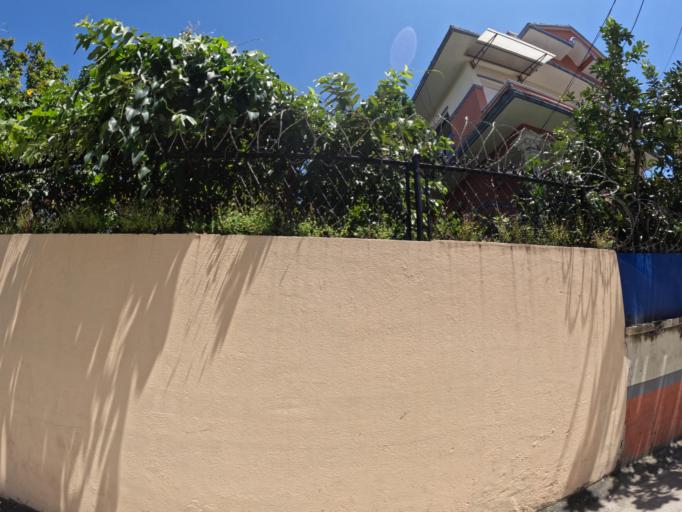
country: NP
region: Central Region
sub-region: Bagmati Zone
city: Kathmandu
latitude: 27.7434
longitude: 85.3260
